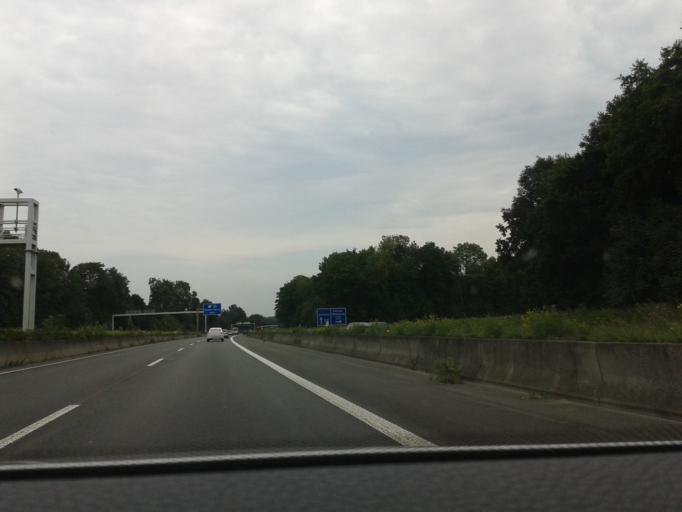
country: DE
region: North Rhine-Westphalia
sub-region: Regierungsbezirk Arnsberg
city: Bochum
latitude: 51.4968
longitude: 7.2722
